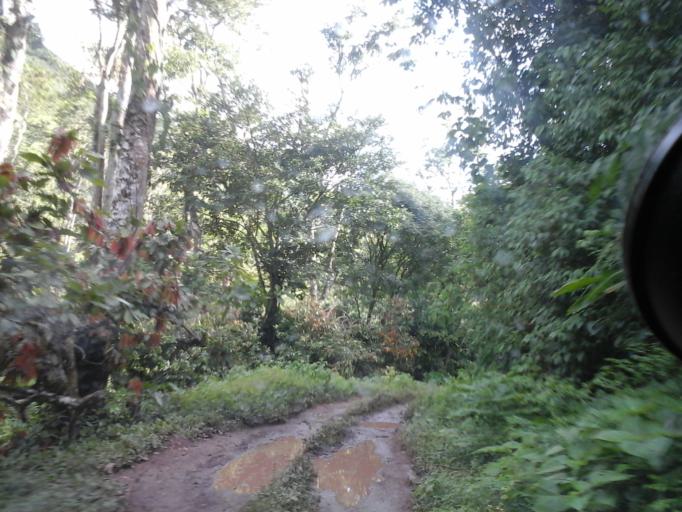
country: CO
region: Cesar
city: San Diego
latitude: 10.2905
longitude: -73.0800
